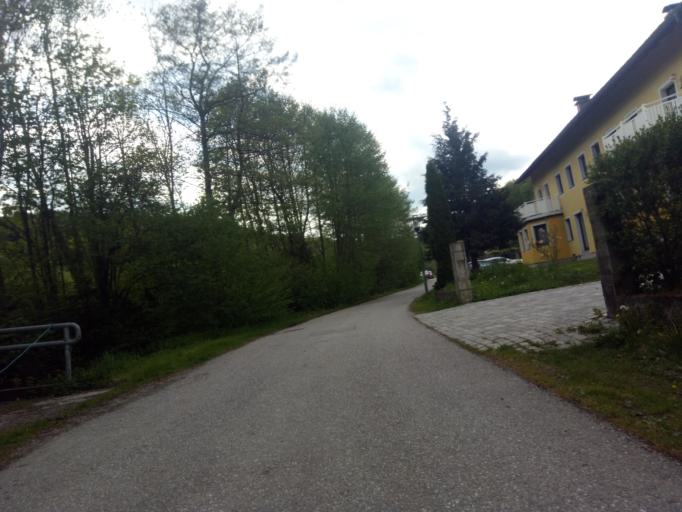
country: AT
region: Lower Austria
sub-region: Politischer Bezirk Wien-Umgebung
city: Wolfsgraben
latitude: 48.1265
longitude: 16.0875
